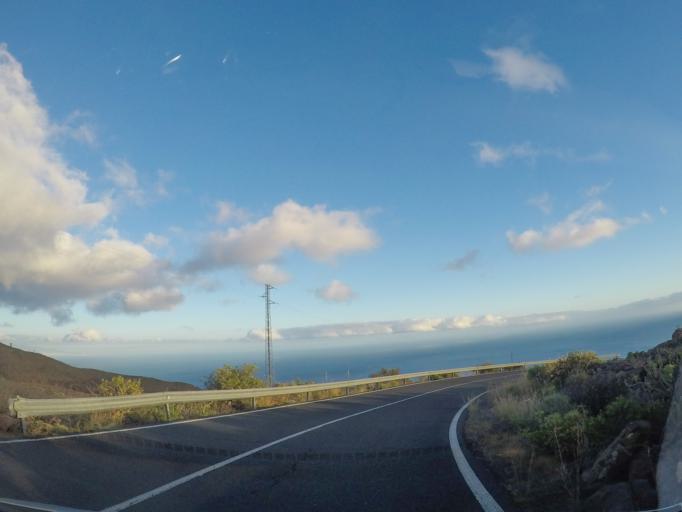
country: ES
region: Canary Islands
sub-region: Provincia de Santa Cruz de Tenerife
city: Alajero
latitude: 28.0508
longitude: -17.2319
